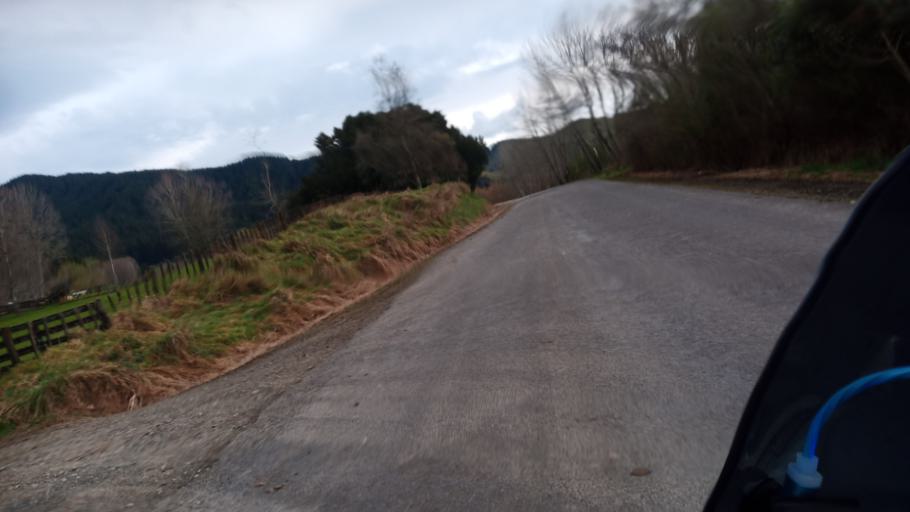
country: NZ
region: Hawke's Bay
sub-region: Wairoa District
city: Wairoa
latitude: -38.8195
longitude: 177.4859
